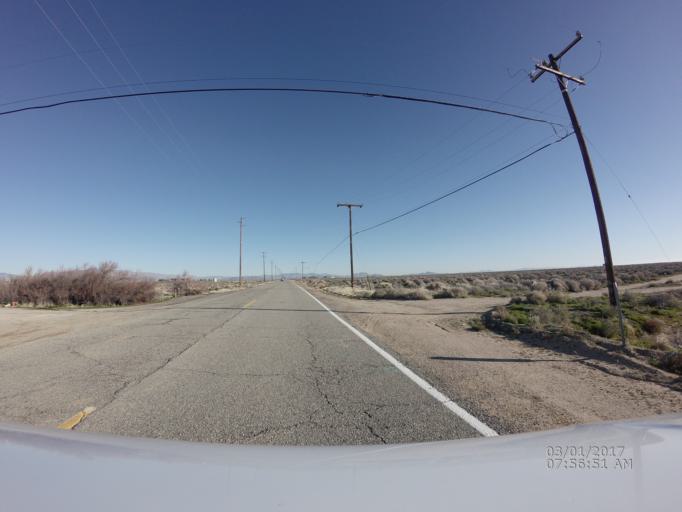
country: US
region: California
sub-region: Los Angeles County
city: Quartz Hill
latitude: 34.7620
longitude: -118.2547
